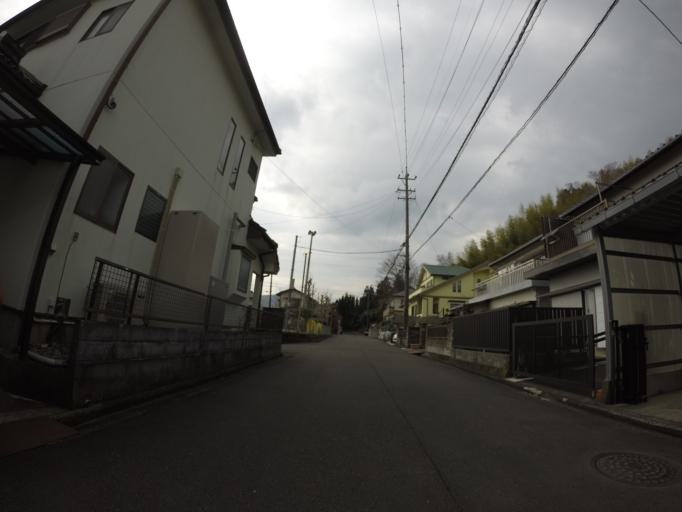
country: JP
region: Shizuoka
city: Shizuoka-shi
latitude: 35.0418
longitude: 138.4616
